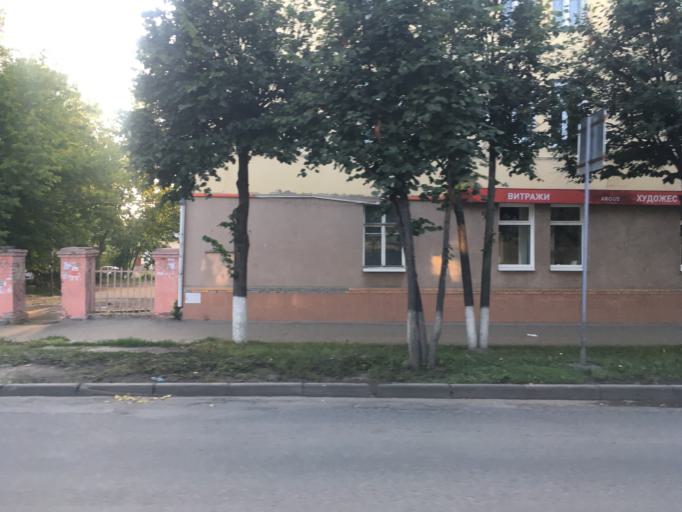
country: RU
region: Mariy-El
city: Yoshkar-Ola
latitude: 56.6453
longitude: 47.8918
